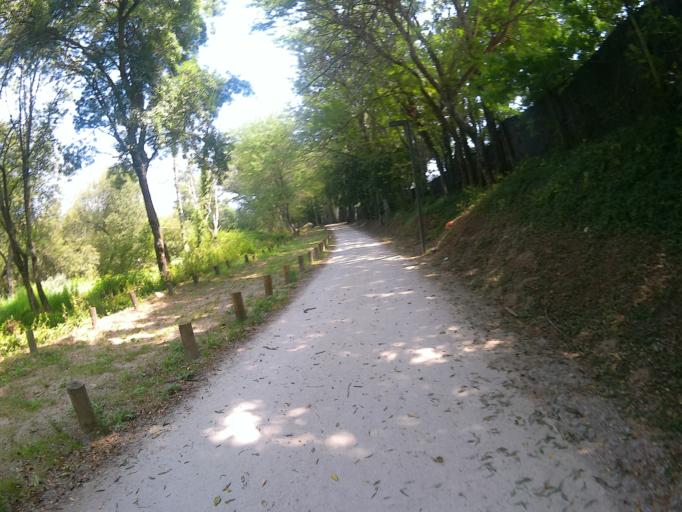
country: PT
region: Viana do Castelo
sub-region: Ponte de Lima
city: Ponte de Lima
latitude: 41.7732
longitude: -8.5839
